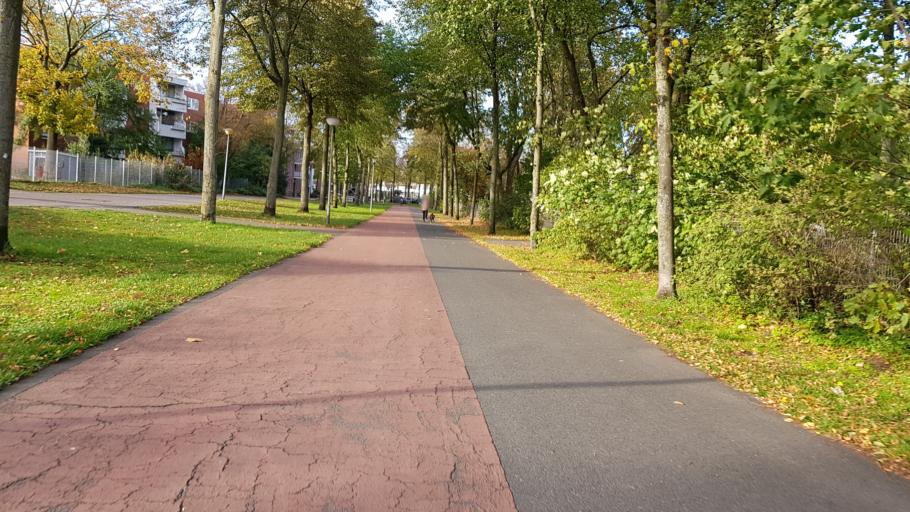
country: DE
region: Bremen
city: Bremen
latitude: 53.1114
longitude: 8.7614
